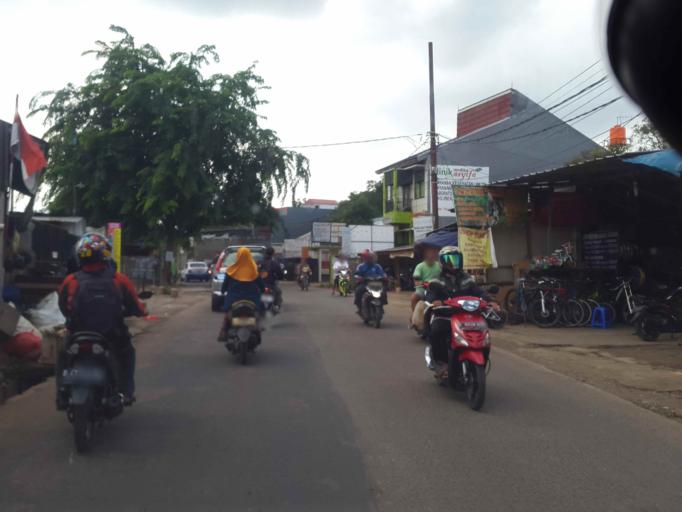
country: ID
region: West Java
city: Cileungsir
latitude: -6.3268
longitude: 106.9467
